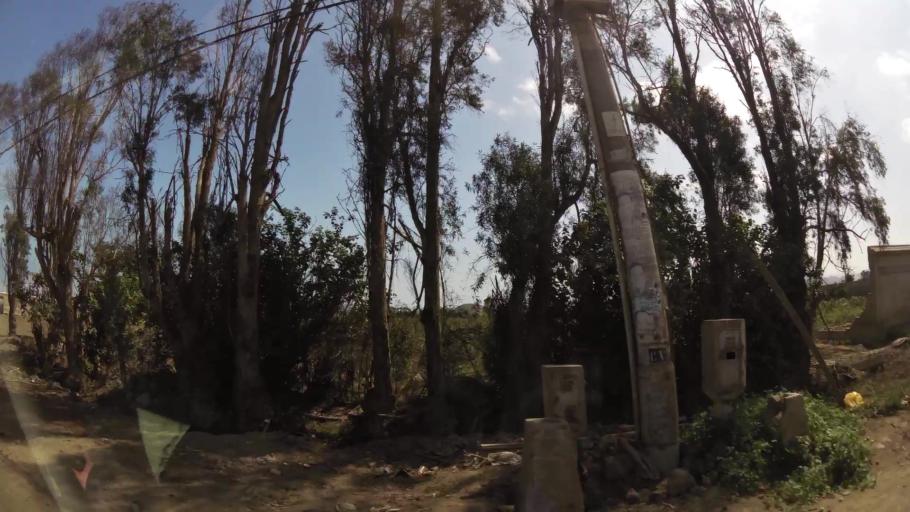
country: PE
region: Lima
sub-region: Provincia de Canete
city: Mala
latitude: -12.6726
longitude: -76.6470
